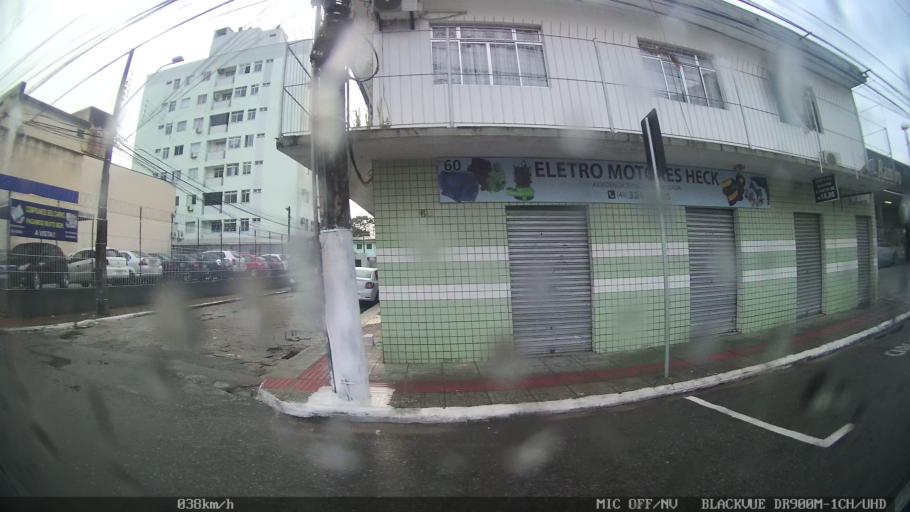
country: BR
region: Santa Catarina
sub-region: Sao Jose
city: Campinas
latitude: -27.5968
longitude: -48.6056
